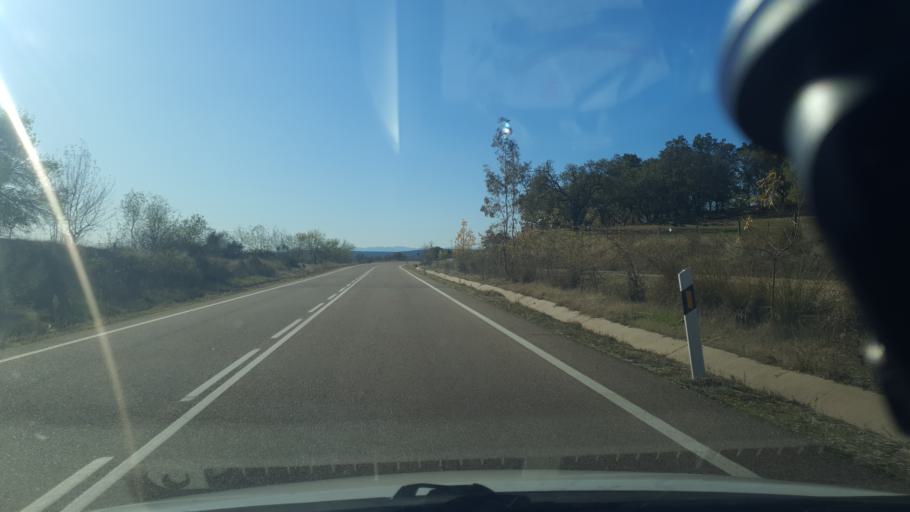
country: ES
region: Castille and Leon
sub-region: Provincia de Avila
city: Poyales del Hoyo
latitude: 40.1508
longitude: -5.1894
